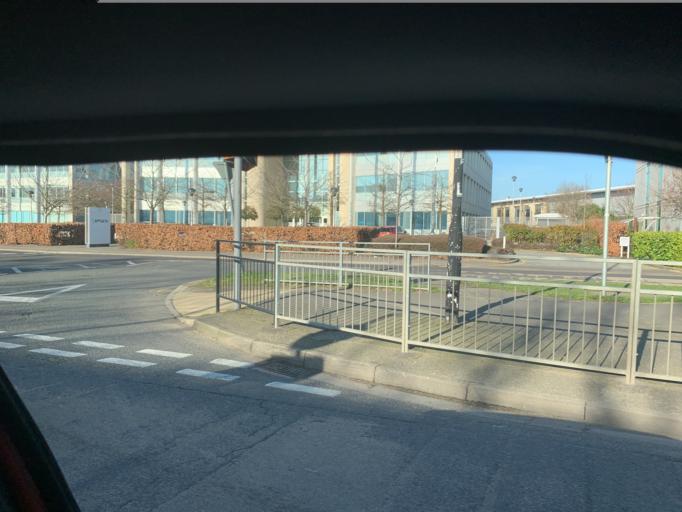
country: GB
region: England
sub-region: Slough
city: Slough
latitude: 51.5141
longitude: -0.6187
